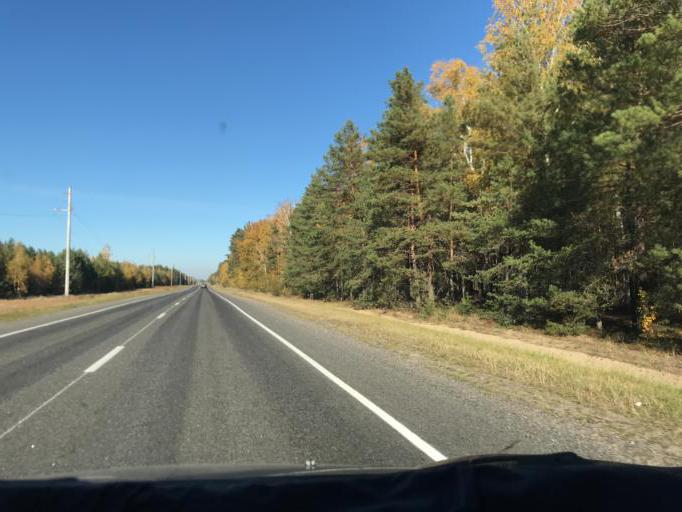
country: BY
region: Gomel
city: Yel'sk
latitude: 51.8864
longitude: 29.2396
